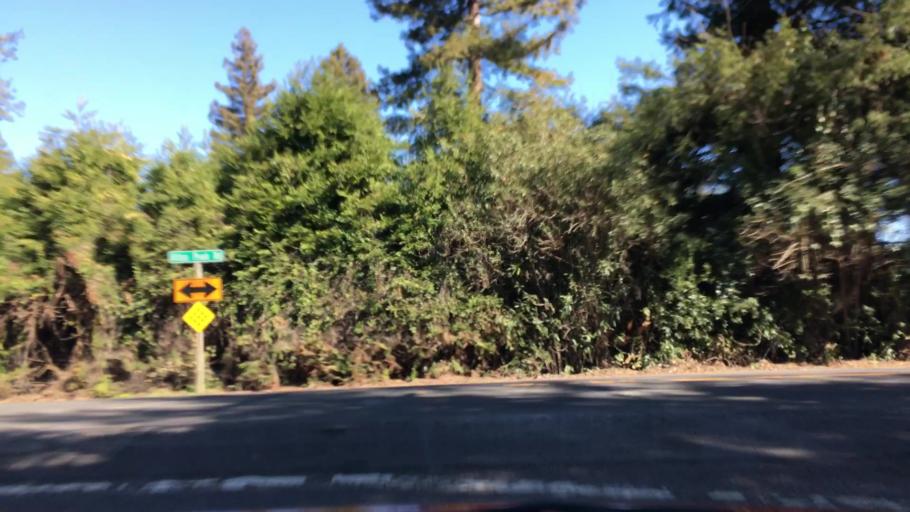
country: US
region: California
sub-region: Napa County
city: Napa
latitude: 38.3437
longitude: -122.2665
